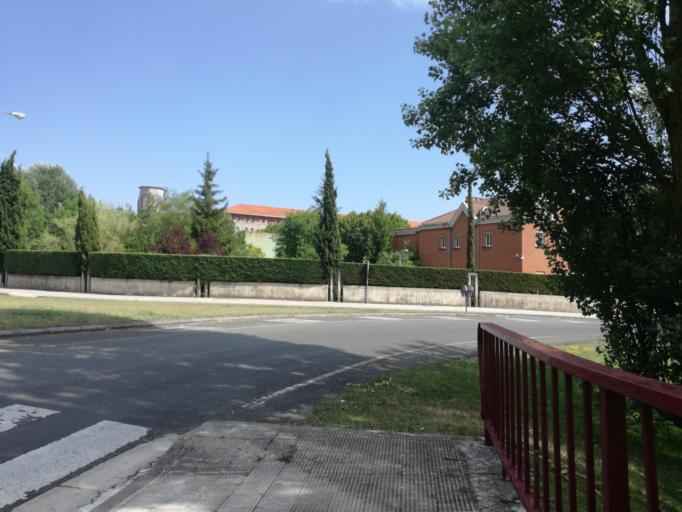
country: ES
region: Basque Country
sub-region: Provincia de Alava
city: Gasteiz / Vitoria
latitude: 42.8522
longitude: -2.6931
